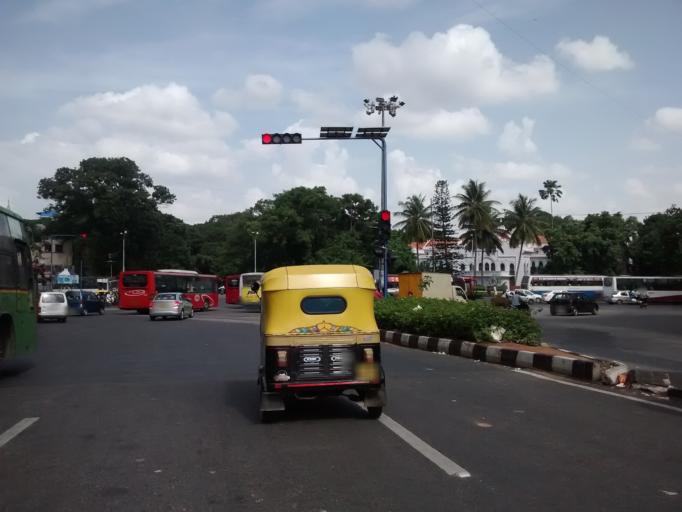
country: IN
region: Karnataka
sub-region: Bangalore Urban
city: Bangalore
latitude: 12.9762
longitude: 77.5869
